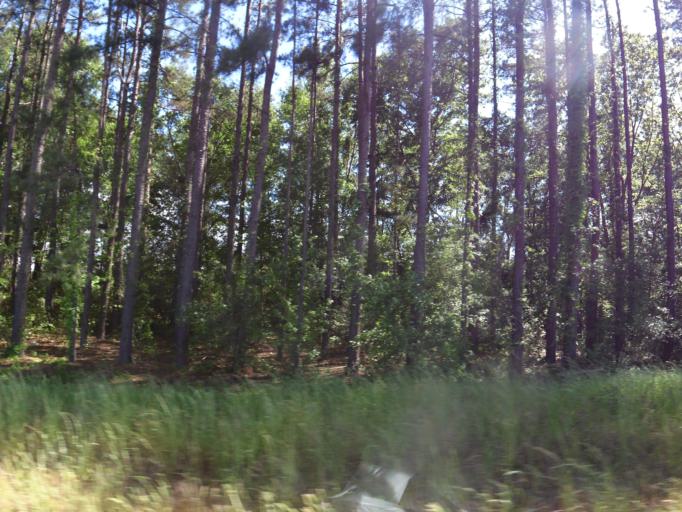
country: US
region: South Carolina
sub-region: Bamberg County
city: Denmark
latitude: 33.3432
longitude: -81.1894
